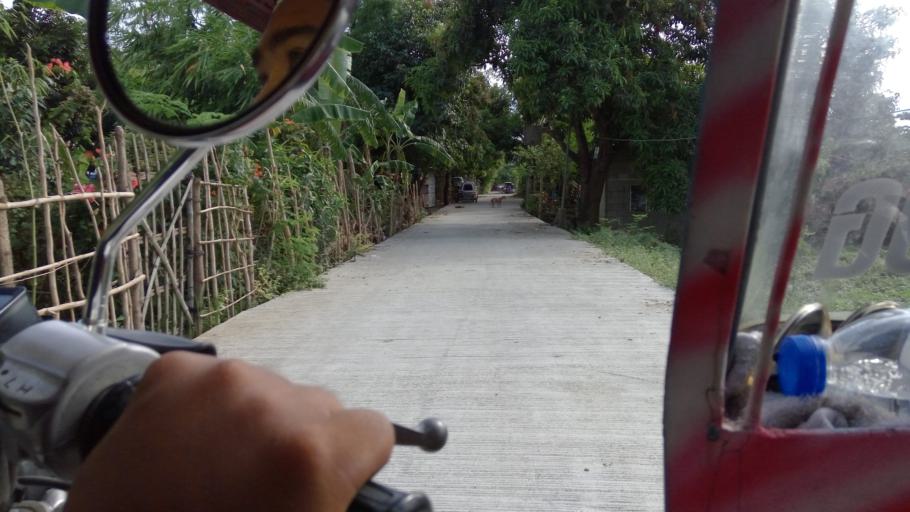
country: PH
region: Ilocos
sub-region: Province of La Union
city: San Eugenio
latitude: 16.3619
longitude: 120.3525
